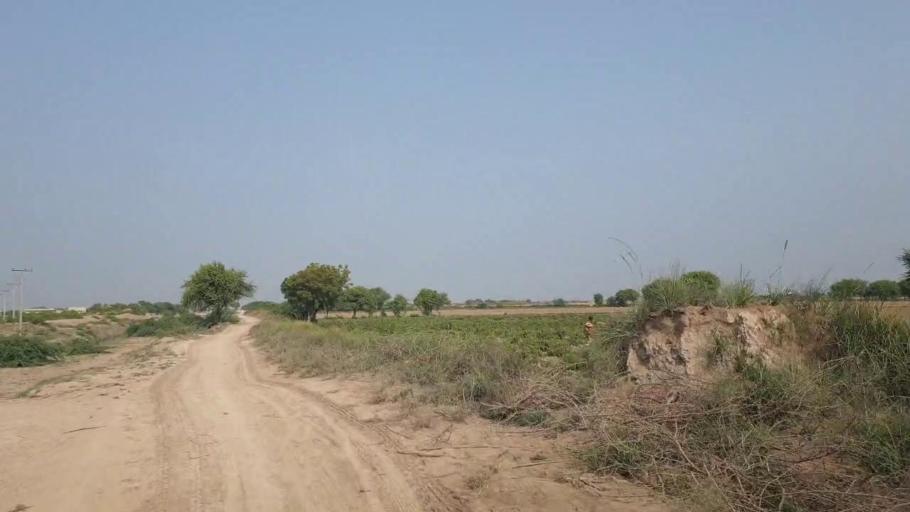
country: PK
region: Sindh
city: Badin
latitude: 24.7004
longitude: 68.7771
